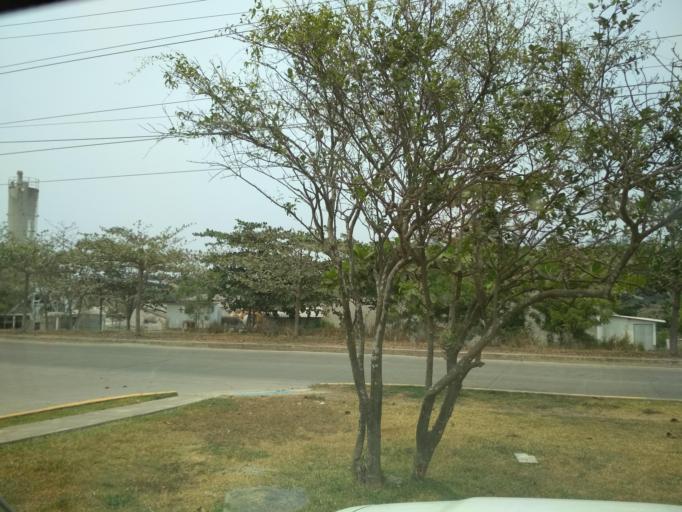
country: MX
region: Veracruz
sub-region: Veracruz
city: Las Amapolas
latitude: 19.1484
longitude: -96.2286
